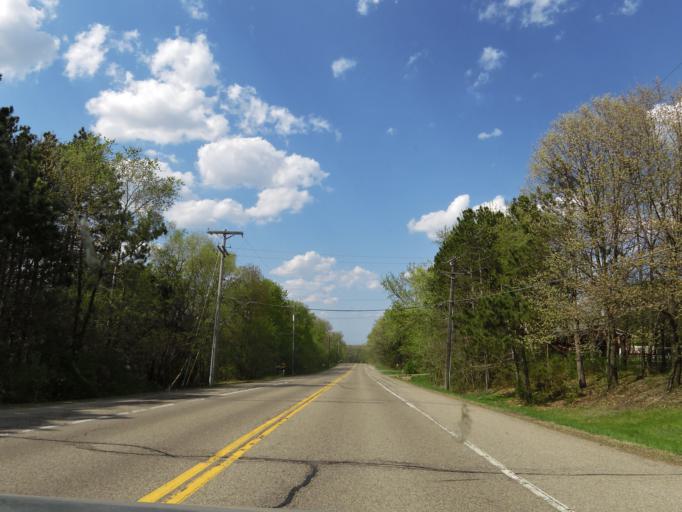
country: US
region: Minnesota
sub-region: Washington County
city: Oak Park Heights
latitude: 45.0031
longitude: -92.8226
